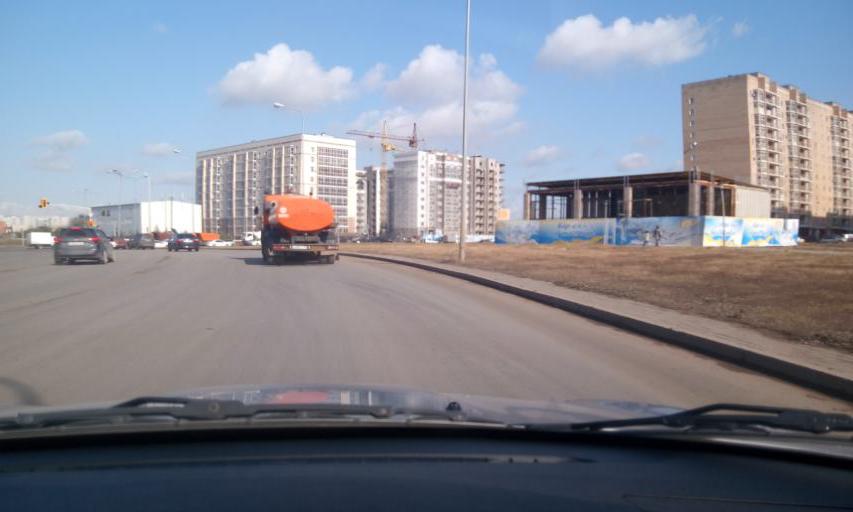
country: KZ
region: Astana Qalasy
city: Astana
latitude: 51.1250
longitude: 71.4869
